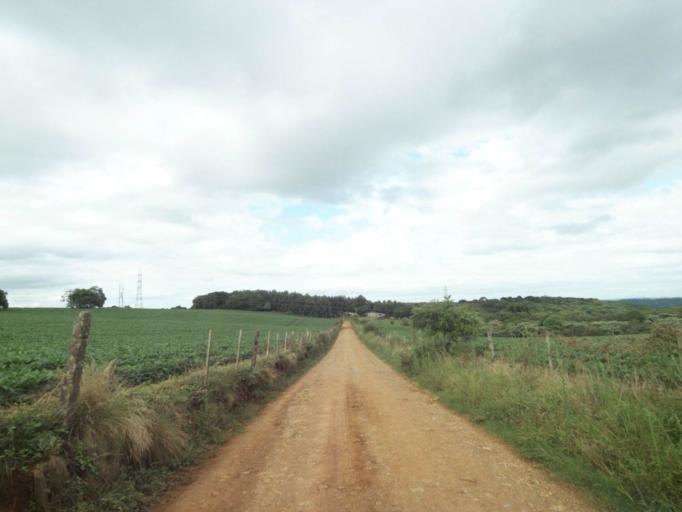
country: BR
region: Rio Grande do Sul
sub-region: Lagoa Vermelha
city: Lagoa Vermelha
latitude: -28.1999
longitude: -51.5133
